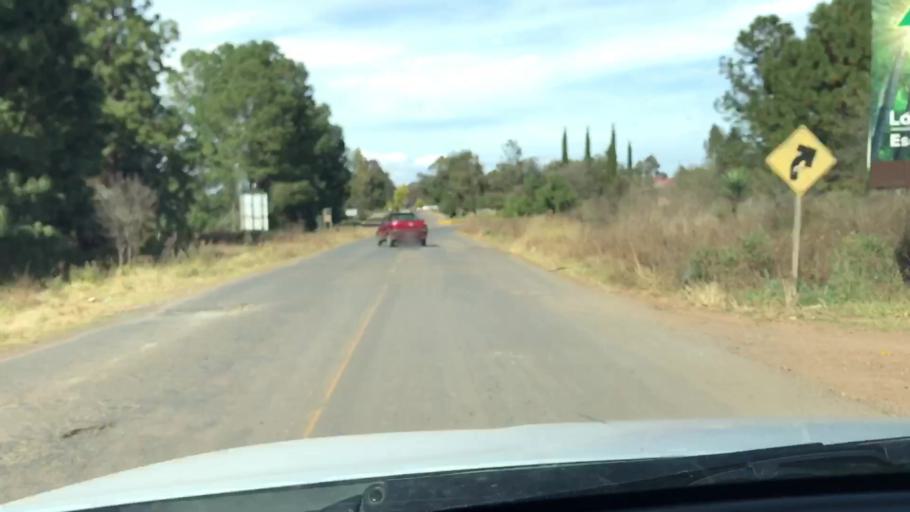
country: MX
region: Jalisco
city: Chiquilistlan
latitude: 20.1244
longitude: -103.7240
